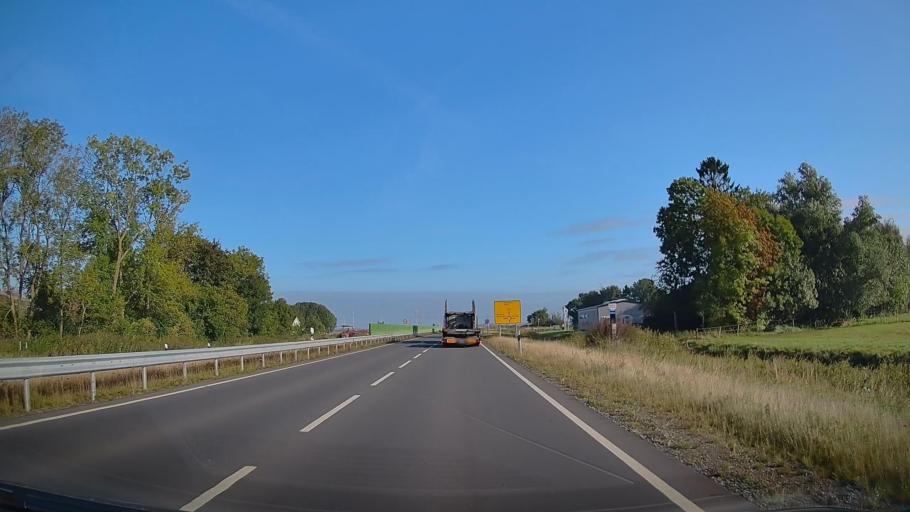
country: DE
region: Lower Saxony
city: Ovelgonne
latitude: 53.3096
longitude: 8.3983
